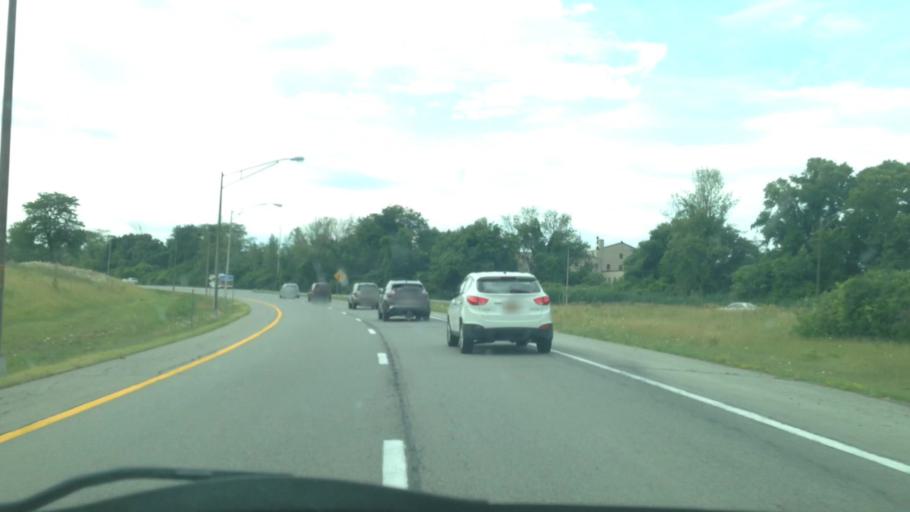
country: US
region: New York
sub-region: Monroe County
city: North Gates
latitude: 43.1547
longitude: -77.6803
